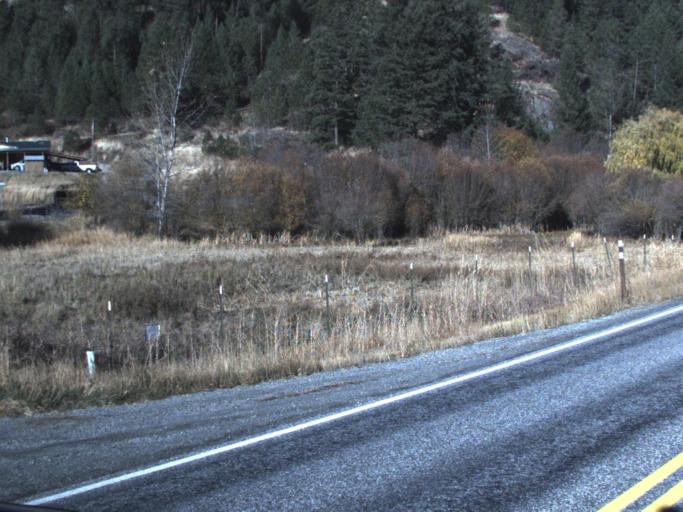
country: US
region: Washington
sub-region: Ferry County
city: Republic
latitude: 48.7917
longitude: -118.6161
